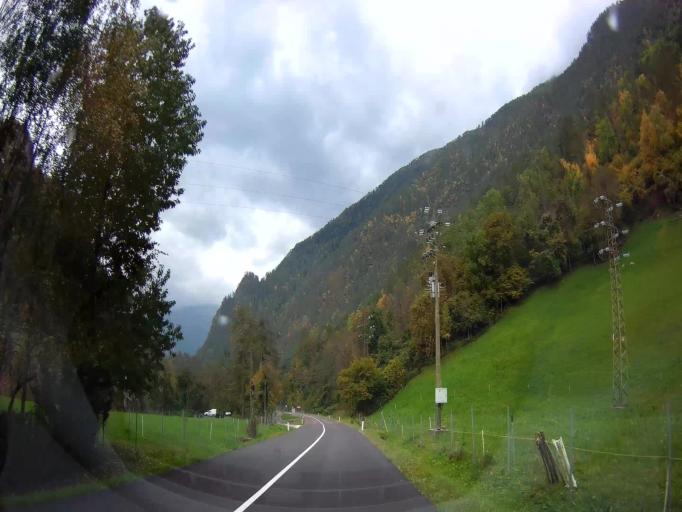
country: IT
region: Trentino-Alto Adige
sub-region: Bolzano
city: Certosa
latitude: 46.6793
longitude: 10.9369
